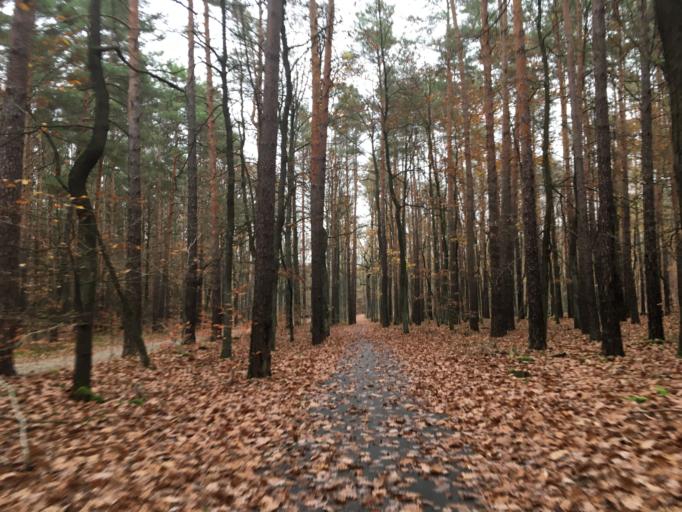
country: DE
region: Brandenburg
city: Mixdorf
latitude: 52.1515
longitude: 14.4303
